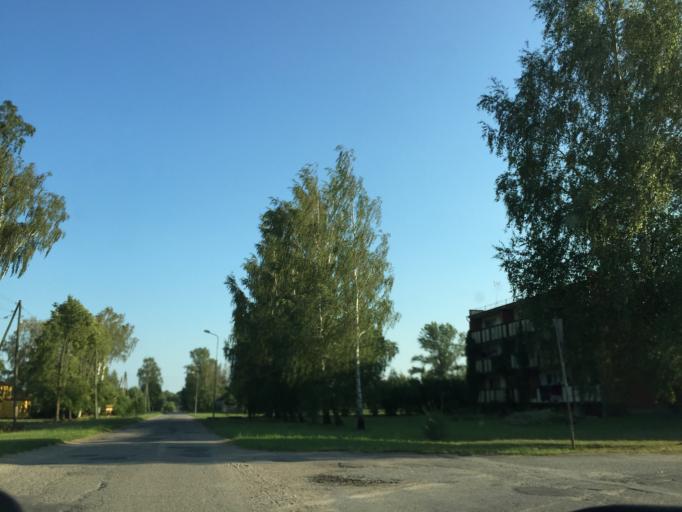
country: LV
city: Tervete
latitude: 56.4357
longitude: 23.4797
